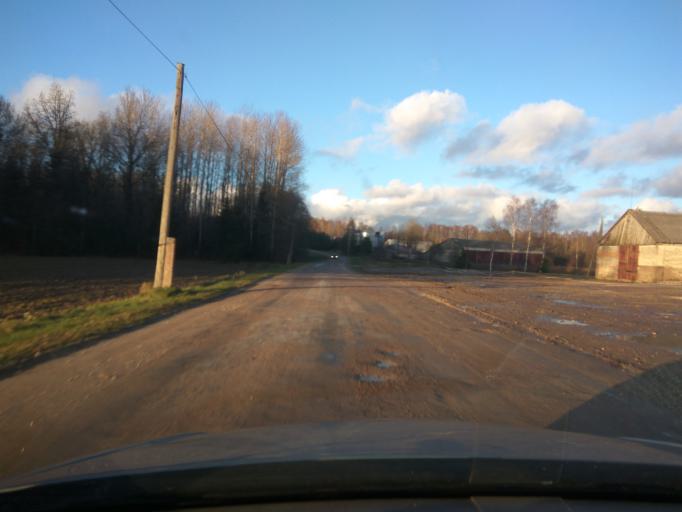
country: LV
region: Aizpute
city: Aizpute
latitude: 56.8266
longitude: 21.7750
